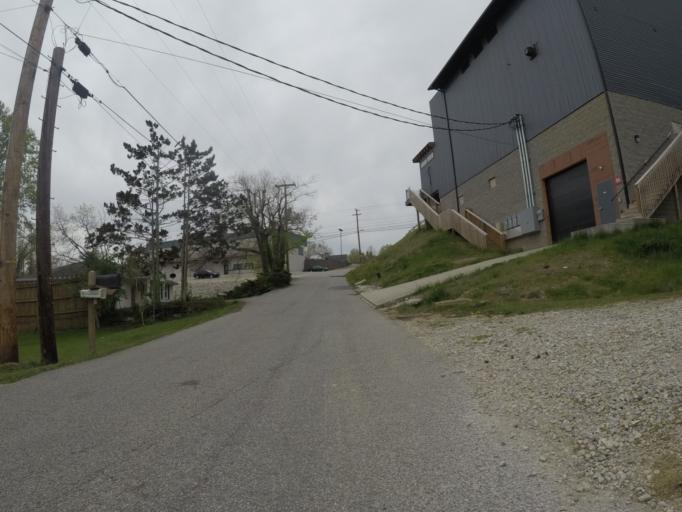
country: US
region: West Virginia
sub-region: Cabell County
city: Pea Ridge
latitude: 38.4121
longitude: -82.3366
